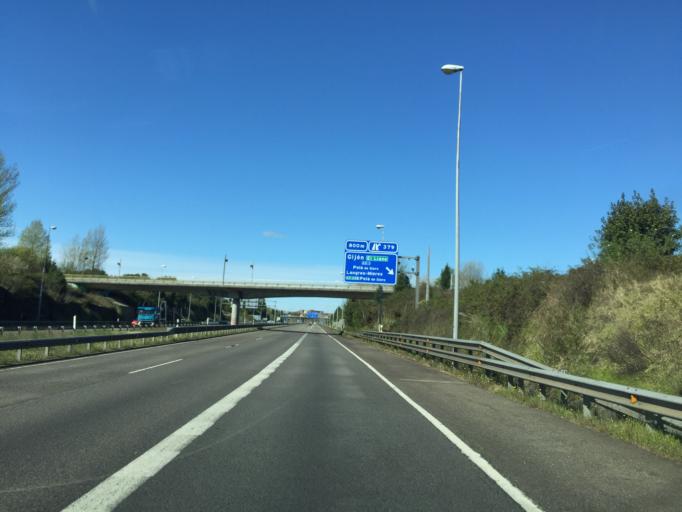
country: ES
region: Asturias
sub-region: Province of Asturias
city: Gijon
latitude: 43.5223
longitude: -5.6418
